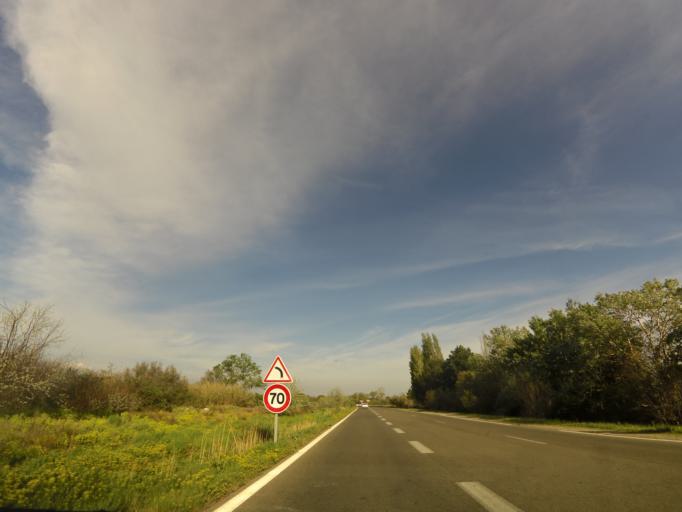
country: FR
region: Languedoc-Roussillon
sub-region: Departement de l'Herault
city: La Grande-Motte
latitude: 43.5759
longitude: 4.1001
